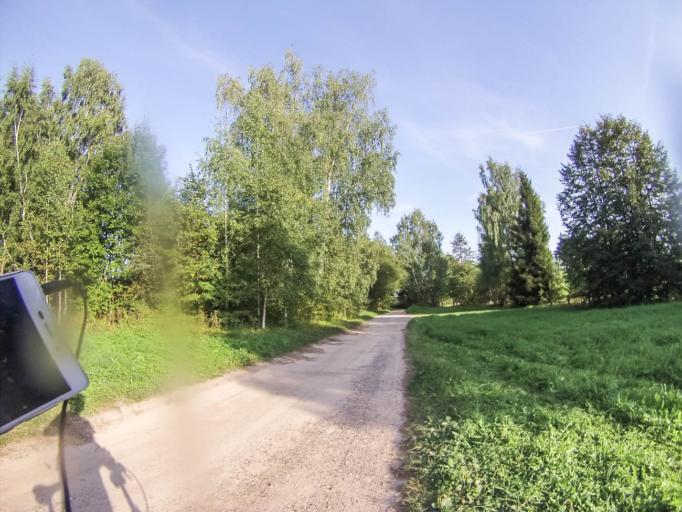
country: RU
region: Jaroslavl
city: Myshkin
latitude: 57.7250
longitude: 38.4218
